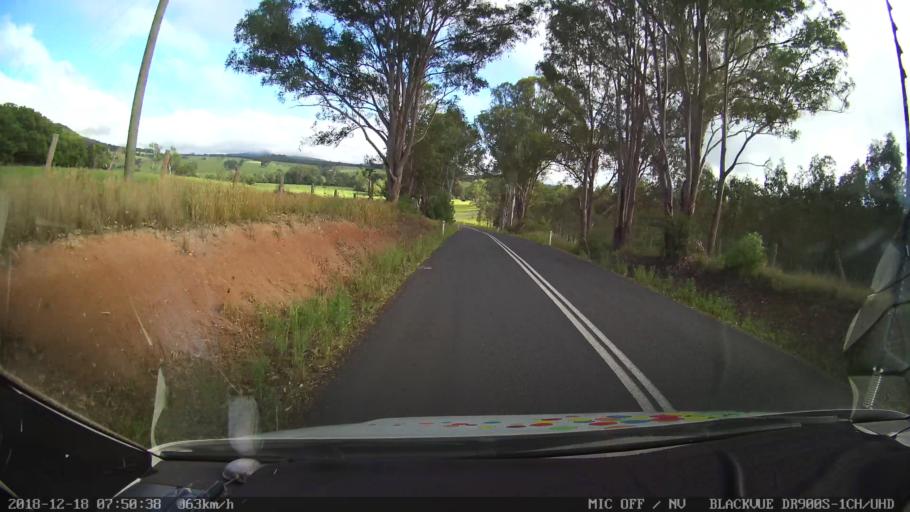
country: AU
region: New South Wales
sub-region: Kyogle
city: Kyogle
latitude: -28.4439
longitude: 152.5745
